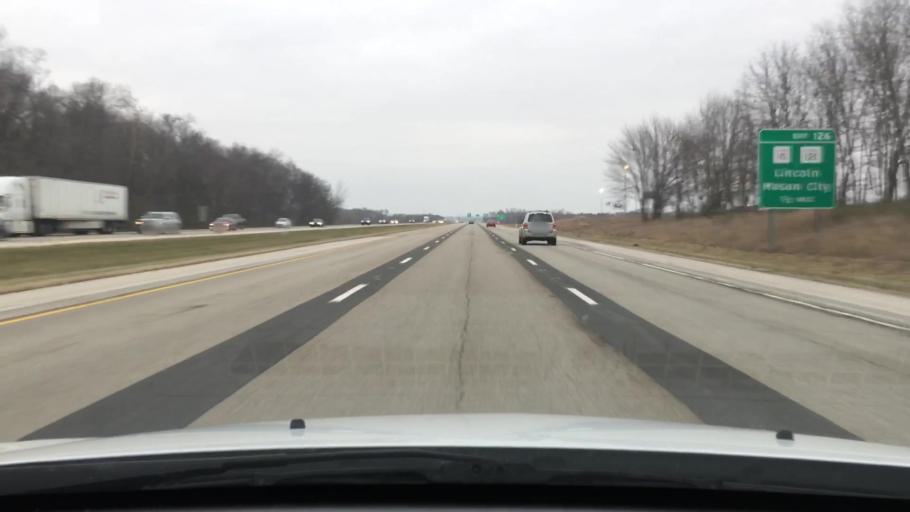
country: US
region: Illinois
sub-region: Logan County
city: Lincoln
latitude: 40.1531
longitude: -89.4173
